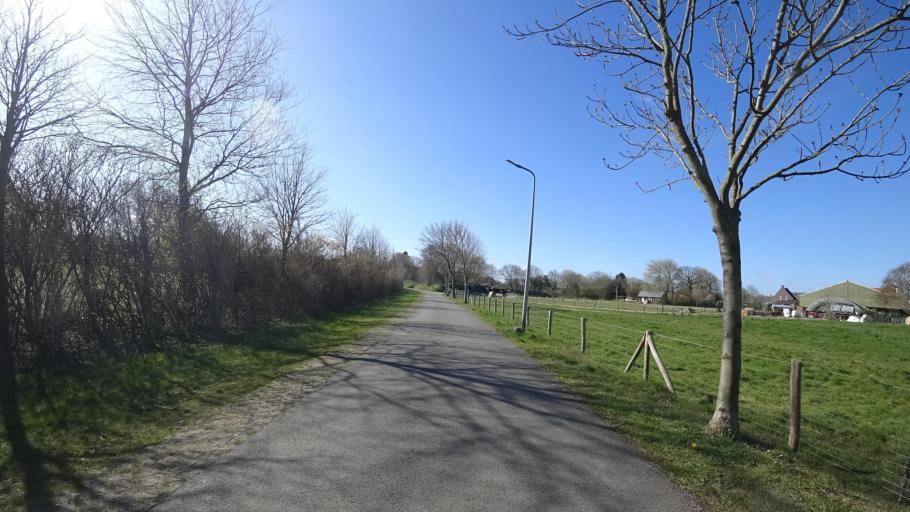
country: NL
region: South Holland
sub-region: Gemeente Goeree-Overflakkee
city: Ouddorp
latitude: 51.8162
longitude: 3.9130
